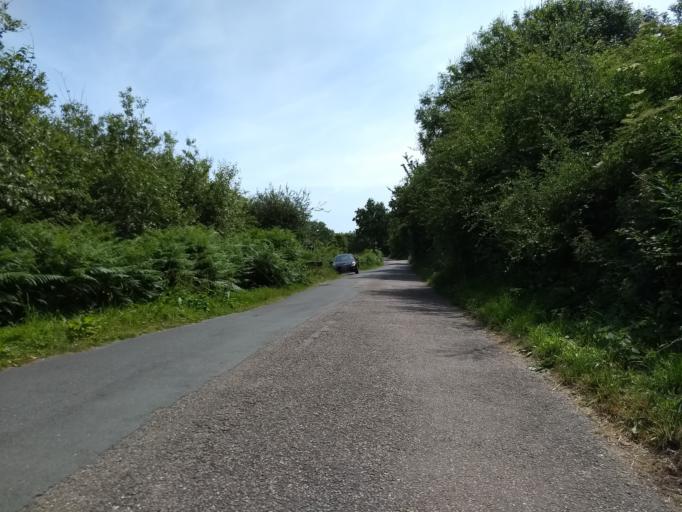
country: GB
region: England
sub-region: Isle of Wight
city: Shanklin
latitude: 50.6183
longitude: -1.1764
